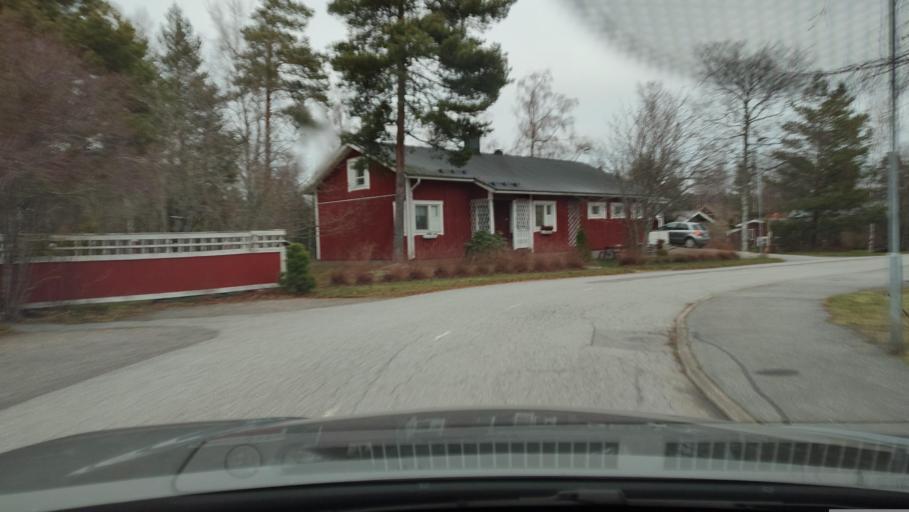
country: FI
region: Ostrobothnia
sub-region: Sydosterbotten
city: Kristinestad
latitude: 62.2817
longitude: 21.3548
